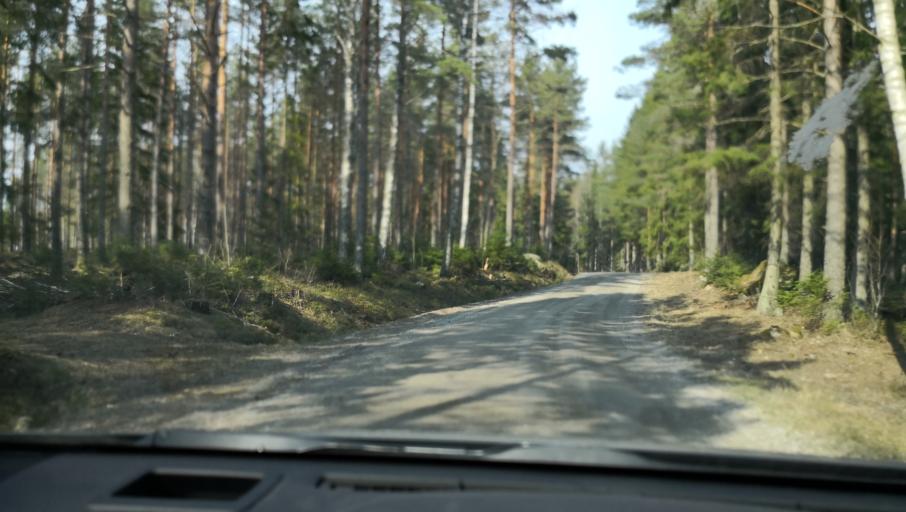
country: SE
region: OErebro
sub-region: Lindesbergs Kommun
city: Frovi
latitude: 59.3575
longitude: 15.4342
